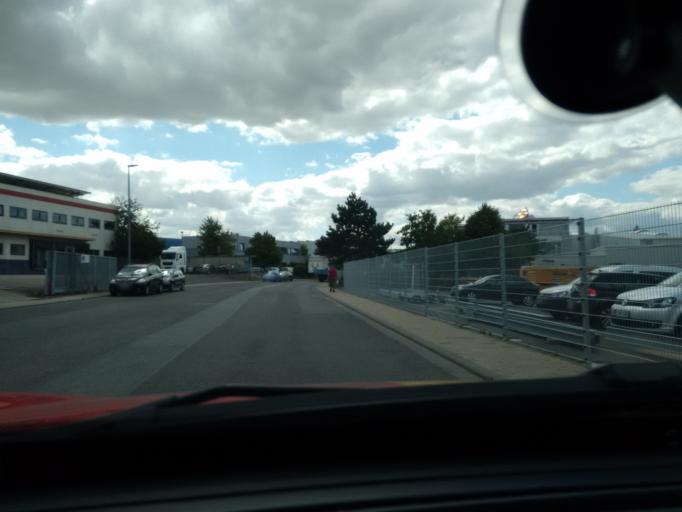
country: DE
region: Rheinland-Pfalz
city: Mainz
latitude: 49.9623
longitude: 8.2626
